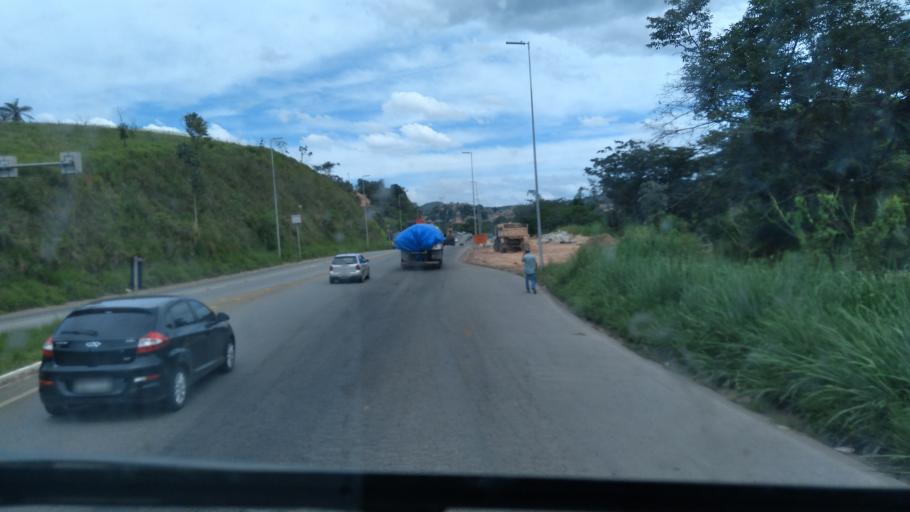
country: BR
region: Minas Gerais
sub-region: Belo Horizonte
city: Belo Horizonte
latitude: -19.8772
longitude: -43.8663
